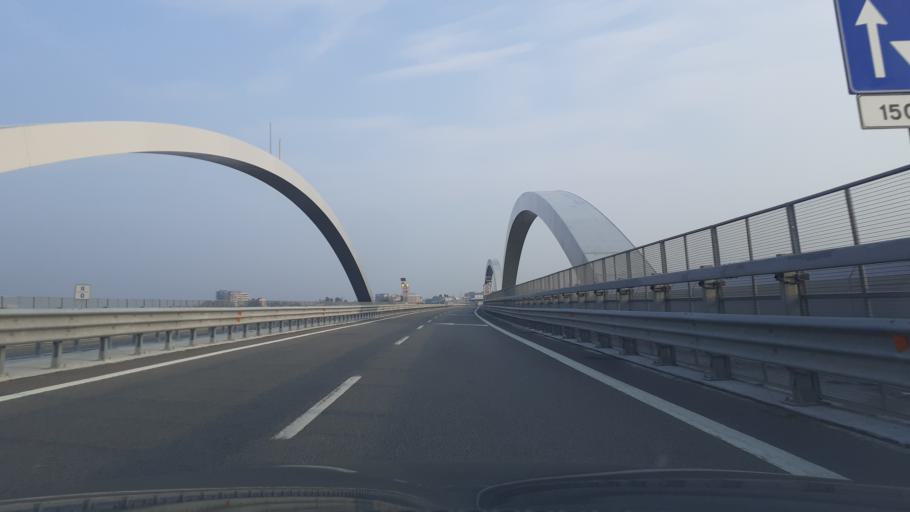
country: IT
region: Lombardy
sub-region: Citta metropolitana di Milano
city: Baranzate
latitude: 45.5169
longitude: 9.1131
